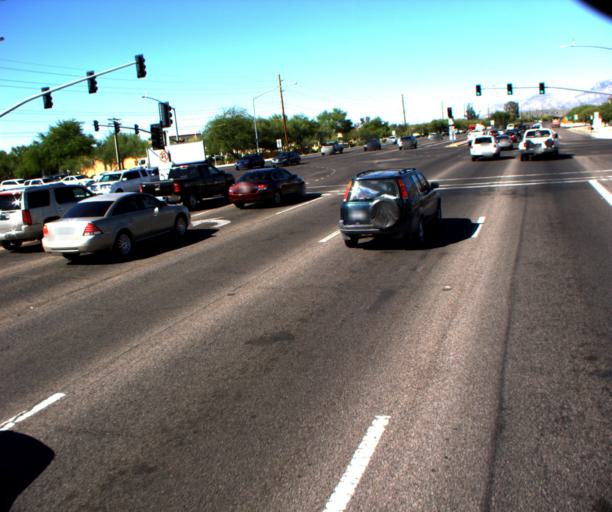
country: US
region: Arizona
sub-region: Pima County
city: Oro Valley
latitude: 32.3996
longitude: -110.9556
